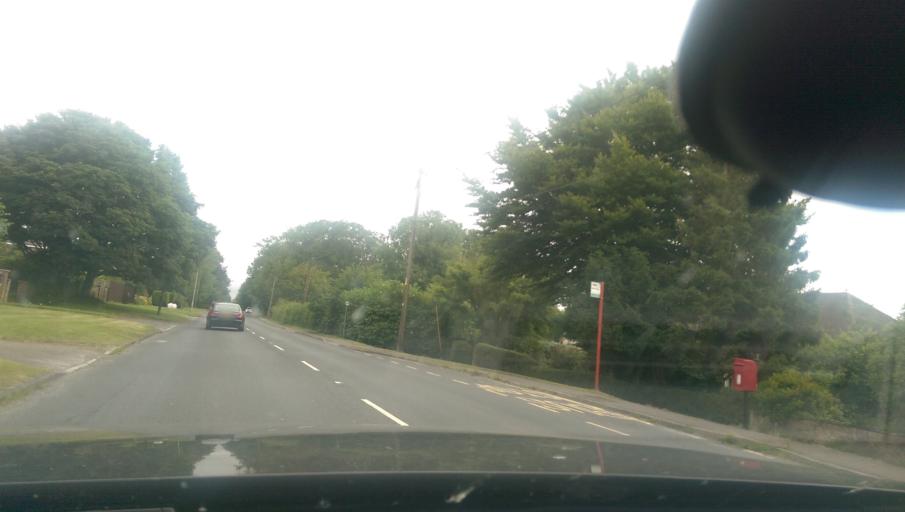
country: GB
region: England
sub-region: Wiltshire
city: Amesbury
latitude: 51.1853
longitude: -1.7832
